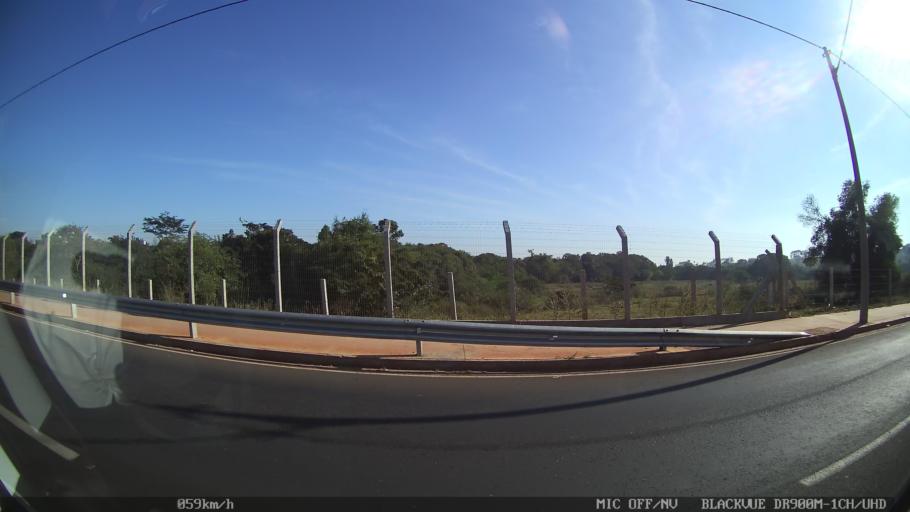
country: BR
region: Sao Paulo
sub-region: Sao Jose Do Rio Preto
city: Sao Jose do Rio Preto
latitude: -20.7612
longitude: -49.3731
